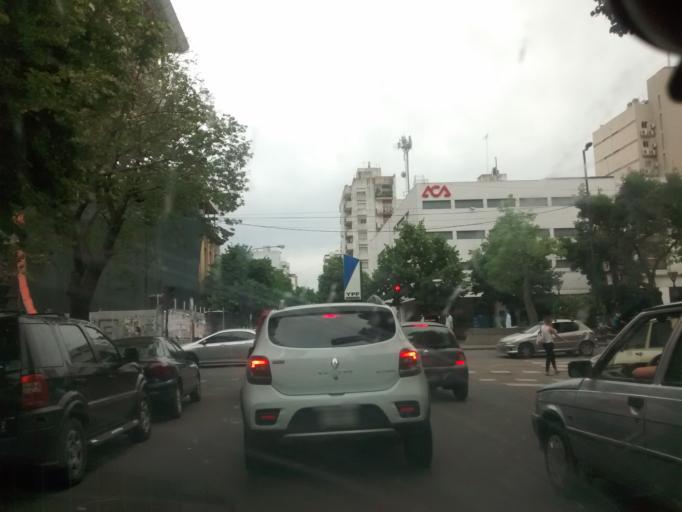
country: AR
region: Buenos Aires
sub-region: Partido de La Plata
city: La Plata
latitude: -34.9175
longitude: -57.9508
